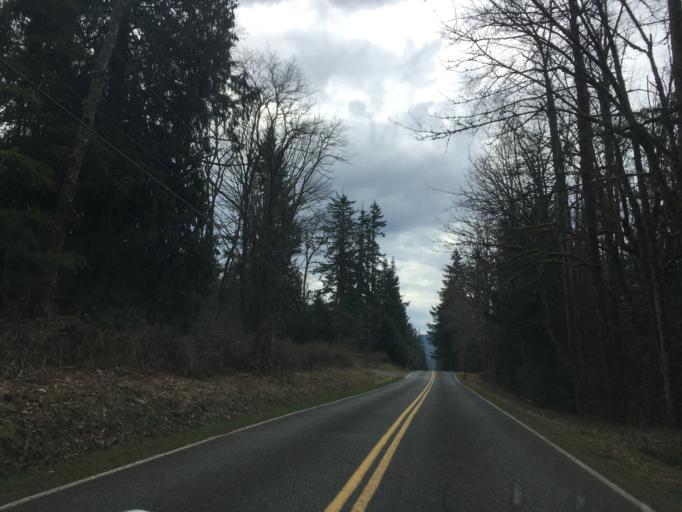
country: US
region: Washington
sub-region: Whatcom County
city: Sudden Valley
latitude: 48.7711
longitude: -122.3553
